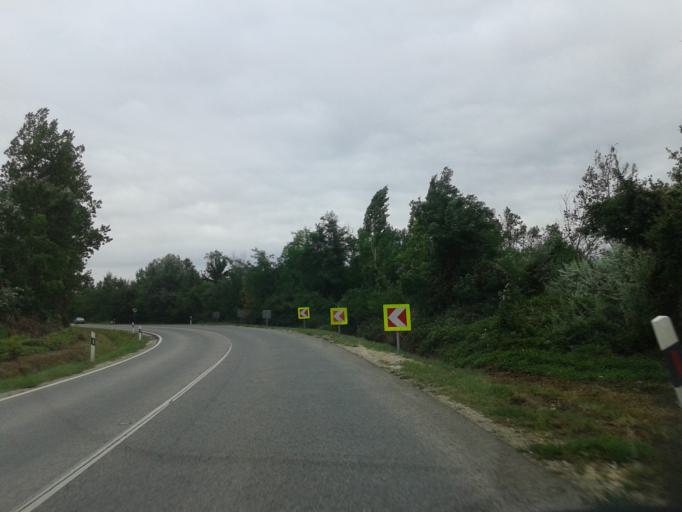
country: HU
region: Pest
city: Dunavarsany
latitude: 47.2774
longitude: 19.0284
